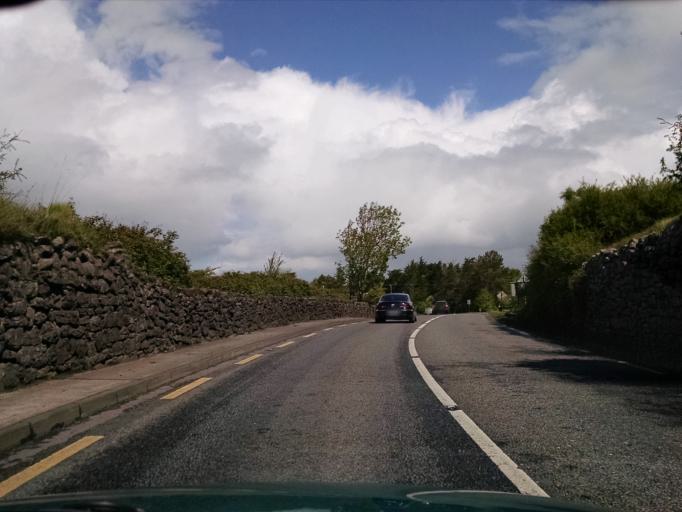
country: IE
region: Connaught
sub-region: County Galway
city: Oranmore
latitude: 53.2338
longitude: -8.8818
